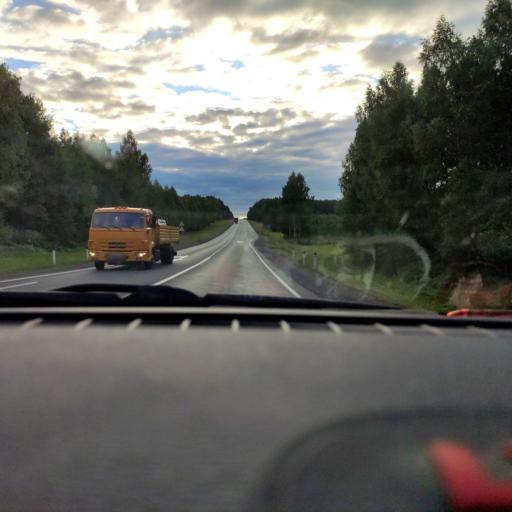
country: RU
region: Perm
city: Pavlovskiy
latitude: 57.9285
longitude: 55.0546
